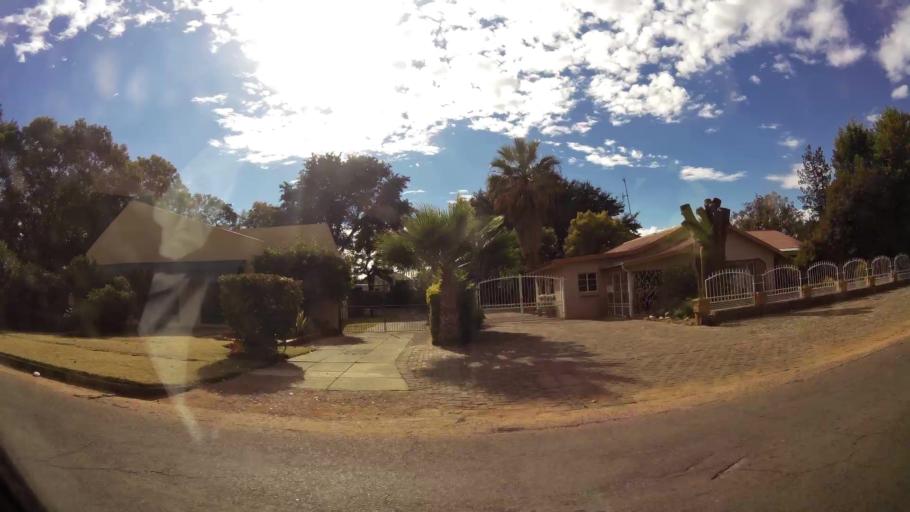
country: ZA
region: Limpopo
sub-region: Waterberg District Municipality
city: Bela-Bela
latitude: -24.8800
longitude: 28.2935
